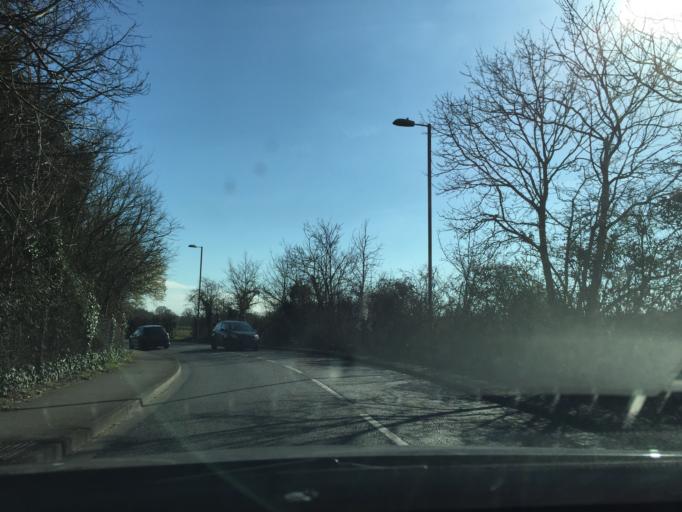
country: GB
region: England
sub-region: Hampshire
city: Hayling Island
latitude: 50.8091
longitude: -0.9774
